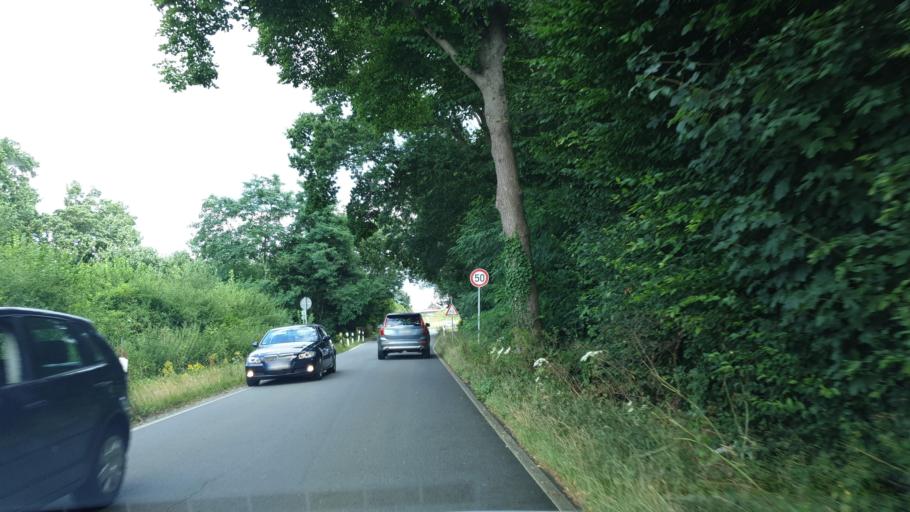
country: DE
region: North Rhine-Westphalia
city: Bad Oeynhausen
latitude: 52.2103
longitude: 8.7510
